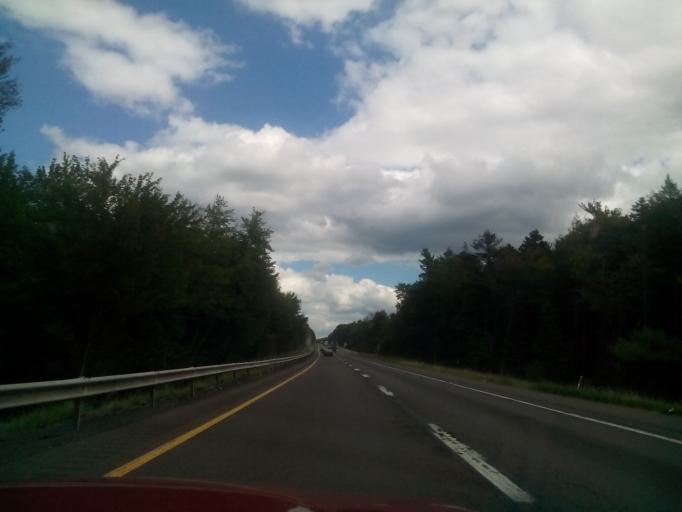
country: US
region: Pennsylvania
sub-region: Carbon County
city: Towamensing Trails
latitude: 41.0758
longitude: -75.5585
